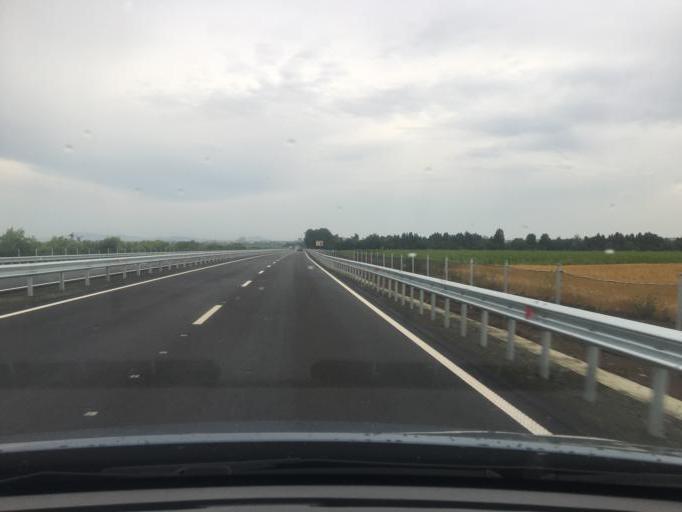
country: BG
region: Burgas
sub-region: Obshtina Pomorie
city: Pomorie
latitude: 42.6023
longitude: 27.6185
